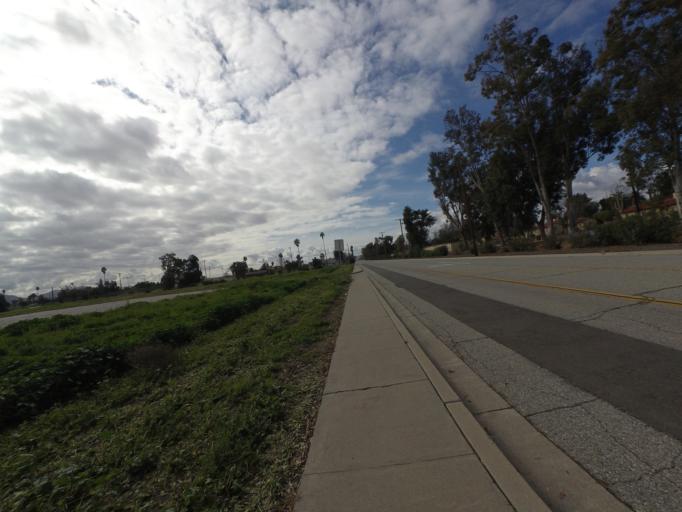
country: US
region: California
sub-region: Riverside County
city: March Air Force Base
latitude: 33.9003
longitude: -117.2523
